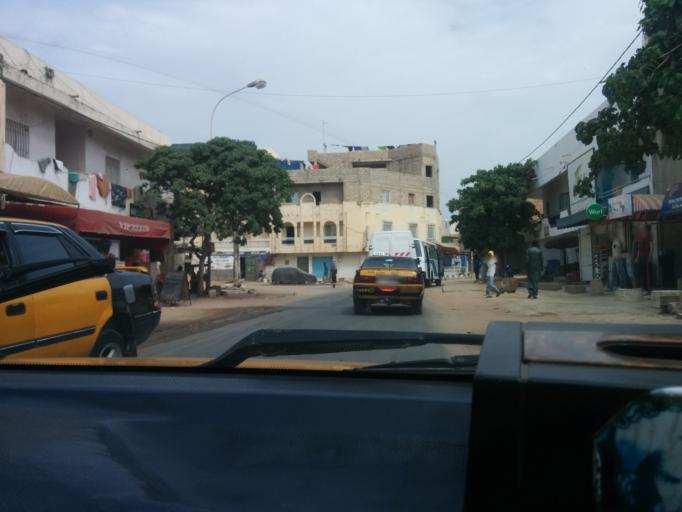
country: SN
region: Dakar
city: Pikine
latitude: 14.7599
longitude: -17.4338
